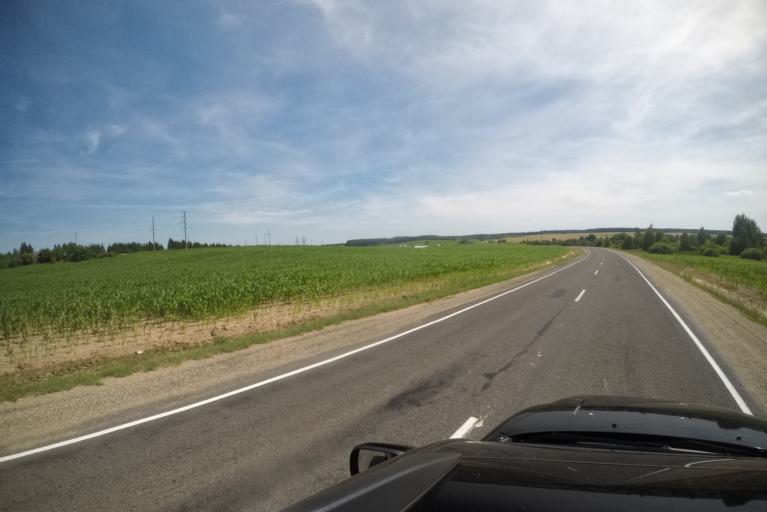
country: BY
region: Grodnenskaya
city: Hal'shany
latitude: 54.2666
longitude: 25.9887
